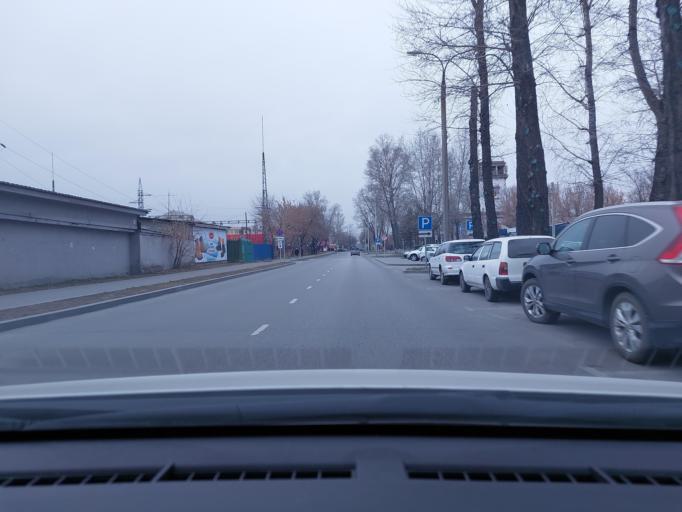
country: RU
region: Irkutsk
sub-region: Irkutskiy Rayon
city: Irkutsk
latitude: 52.3438
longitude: 104.2284
